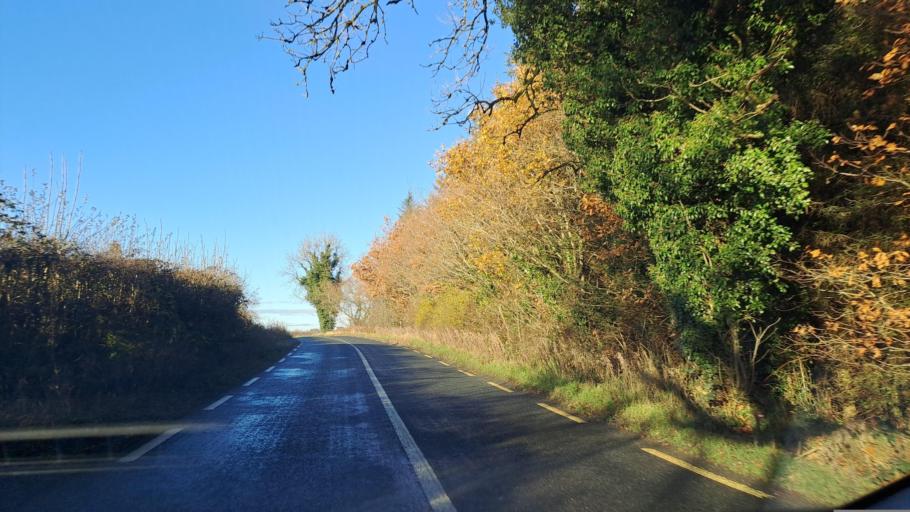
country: IE
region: Ulster
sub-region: An Cabhan
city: Mullagh
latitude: 53.8605
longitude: -6.9556
